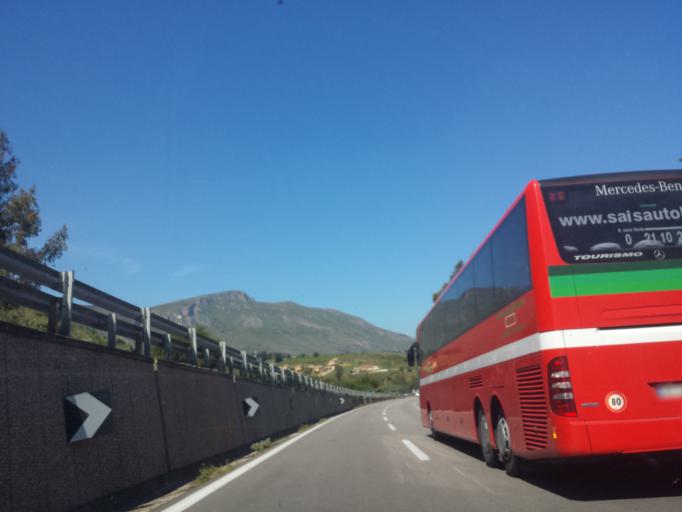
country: IT
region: Sicily
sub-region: Palermo
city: Trabia
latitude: 37.9992
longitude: 13.6394
